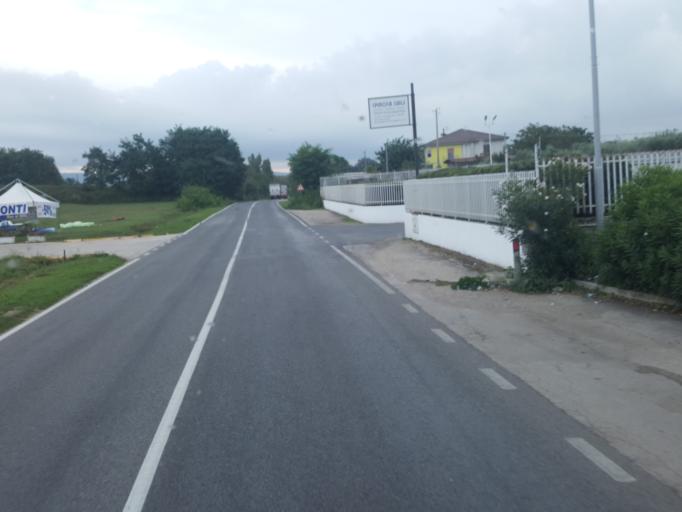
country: IT
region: Campania
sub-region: Provincia di Caserta
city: Sparanise
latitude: 41.1756
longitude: 14.1213
